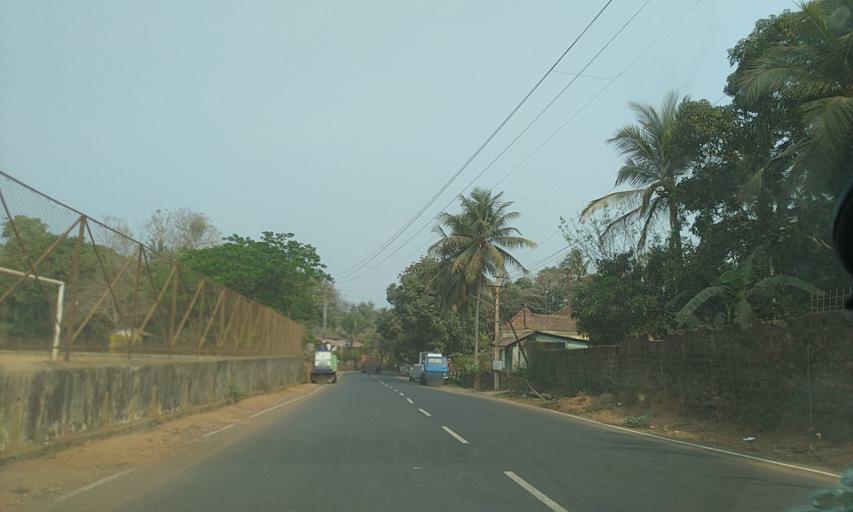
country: IN
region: Goa
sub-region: South Goa
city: Davorlim
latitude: 15.2605
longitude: 74.0463
